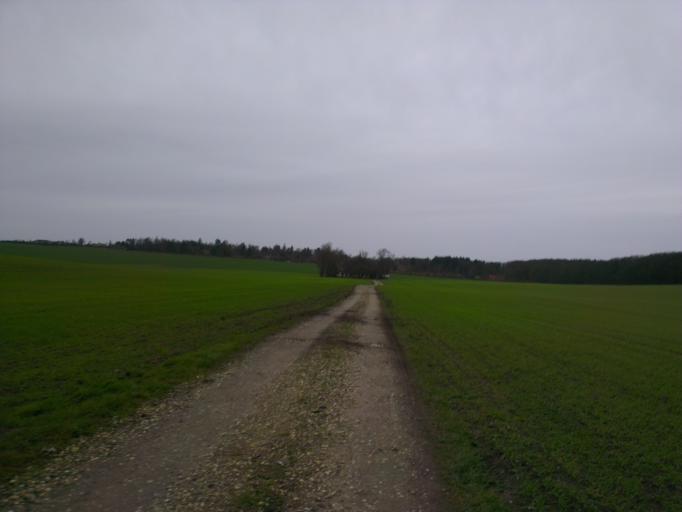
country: DK
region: Capital Region
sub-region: Frederikssund Kommune
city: Jaegerspris
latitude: 55.8426
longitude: 12.0113
